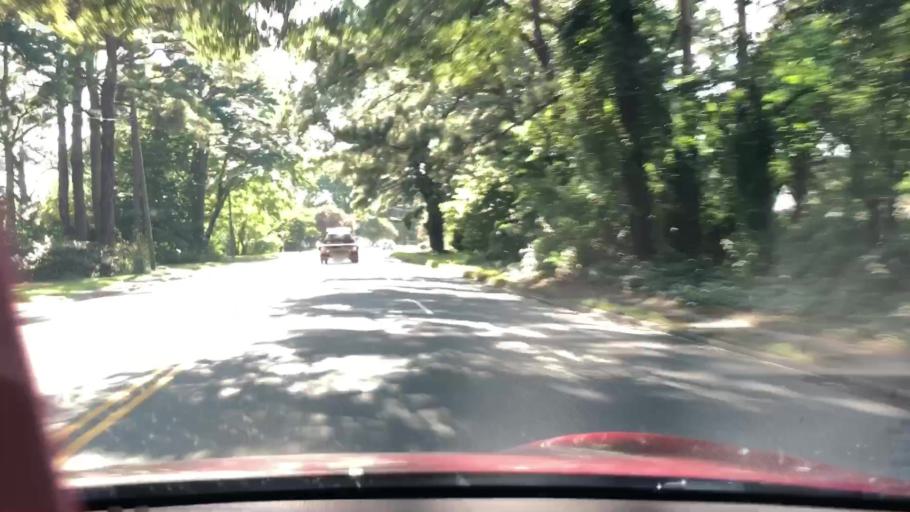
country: US
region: Virginia
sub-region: City of Virginia Beach
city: Virginia Beach
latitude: 36.8427
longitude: -76.0161
